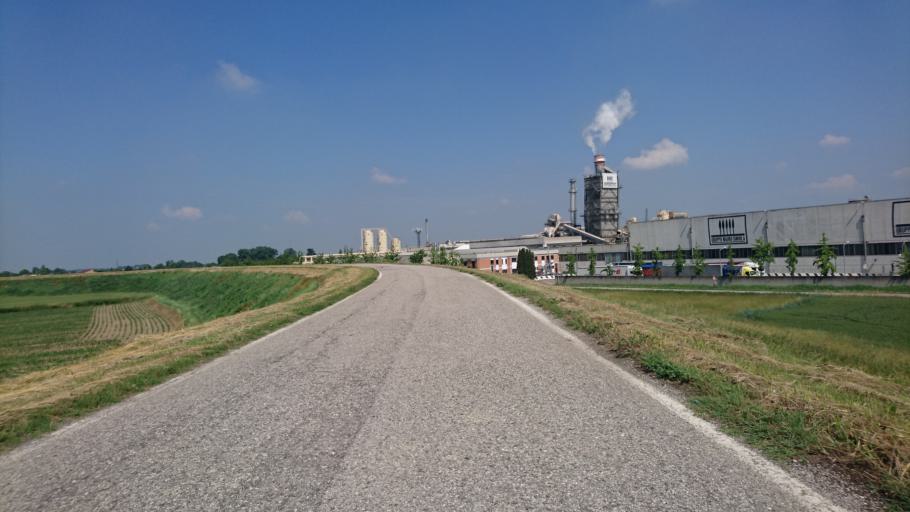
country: IT
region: Lombardy
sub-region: Provincia di Mantova
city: Sustinente
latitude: 45.0670
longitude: 11.0463
